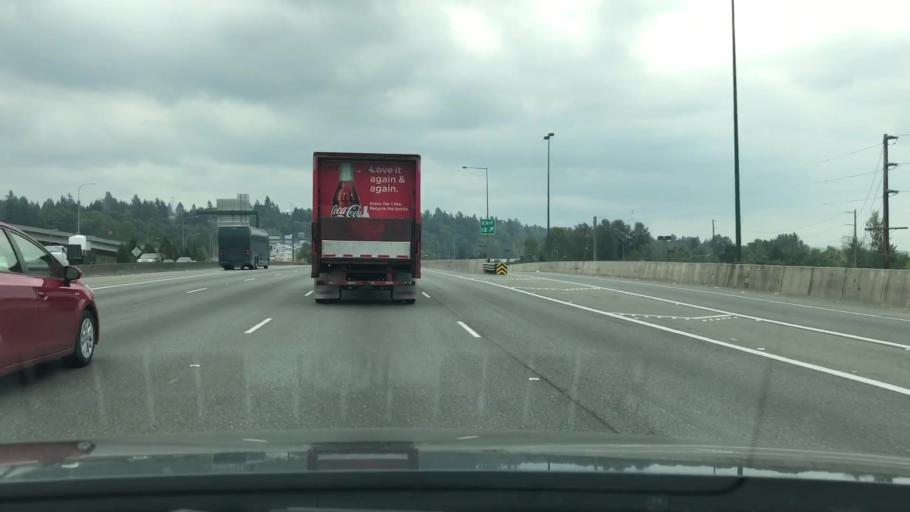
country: US
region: Washington
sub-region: King County
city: Bellevue
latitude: 47.6064
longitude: -122.1881
